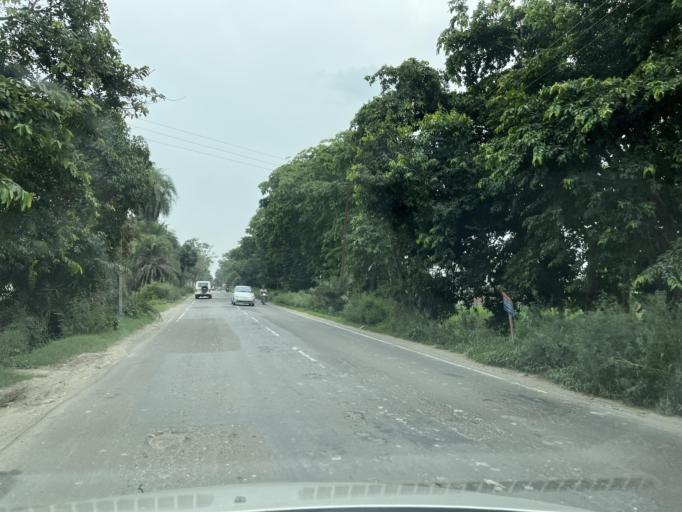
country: IN
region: Uttar Pradesh
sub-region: Rampur
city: Bilaspur
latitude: 29.0300
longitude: 79.2640
